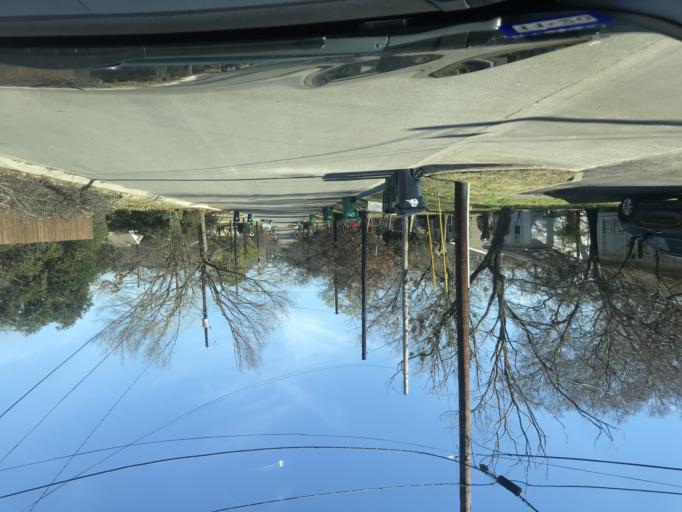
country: US
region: Texas
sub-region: Denton County
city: Denton
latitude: 33.2199
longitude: -97.1503
